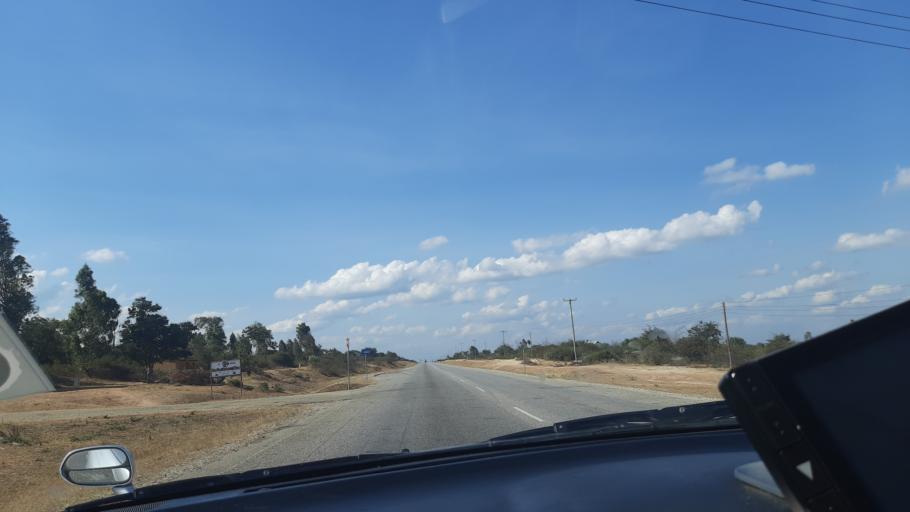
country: TZ
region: Singida
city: Itigi
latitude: -5.5503
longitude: 34.6645
